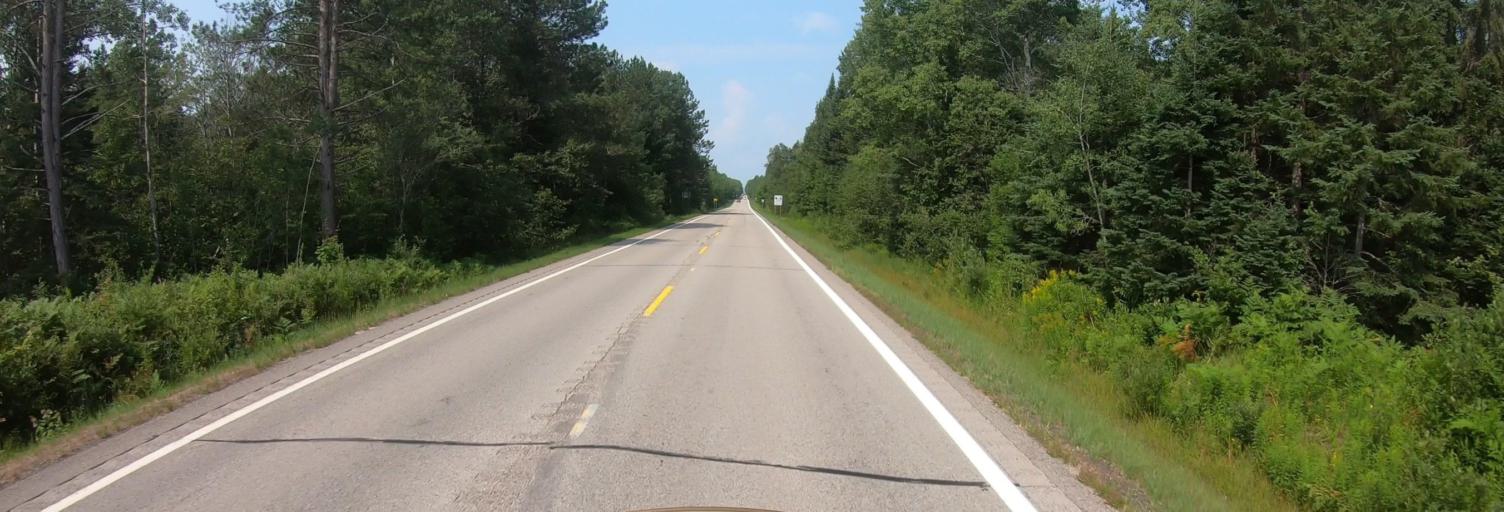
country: US
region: Michigan
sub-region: Luce County
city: Newberry
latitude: 46.5640
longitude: -85.3216
